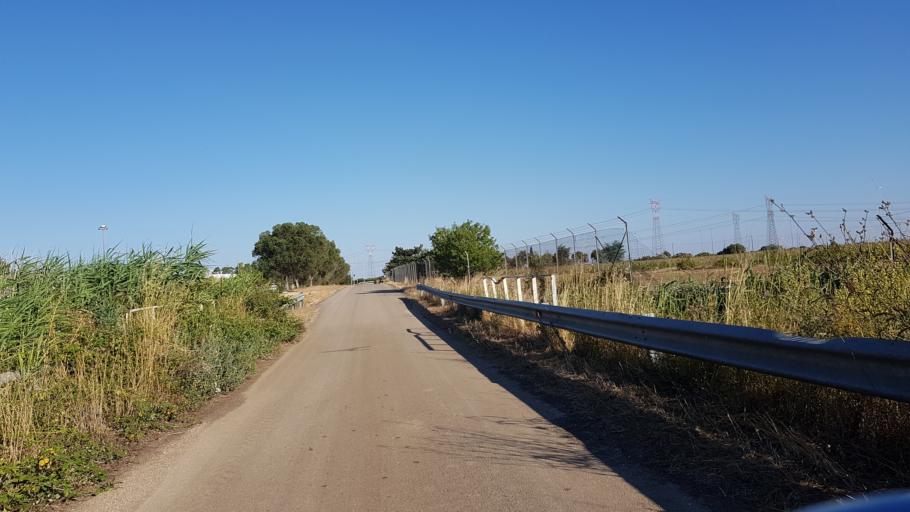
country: IT
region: Apulia
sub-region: Provincia di Brindisi
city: Tuturano
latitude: 40.5617
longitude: 18.0185
